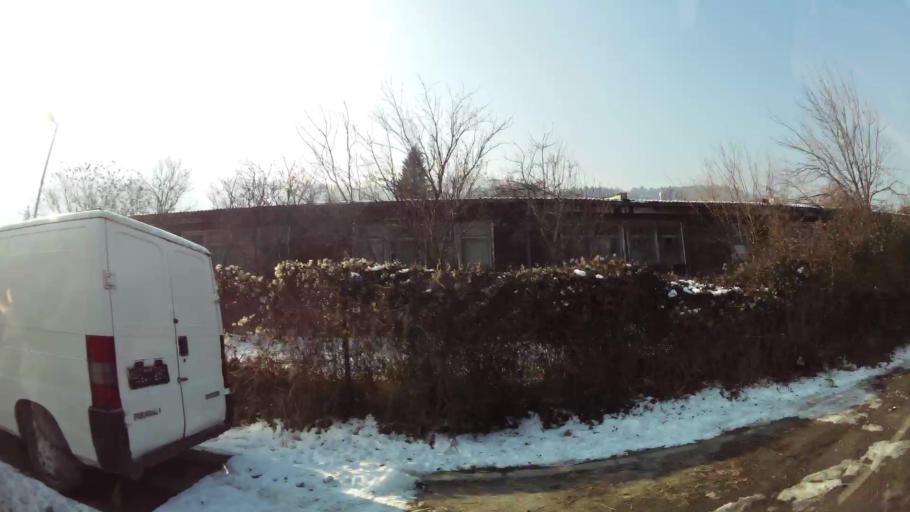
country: MK
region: Karpos
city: Skopje
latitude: 41.9752
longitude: 21.4348
